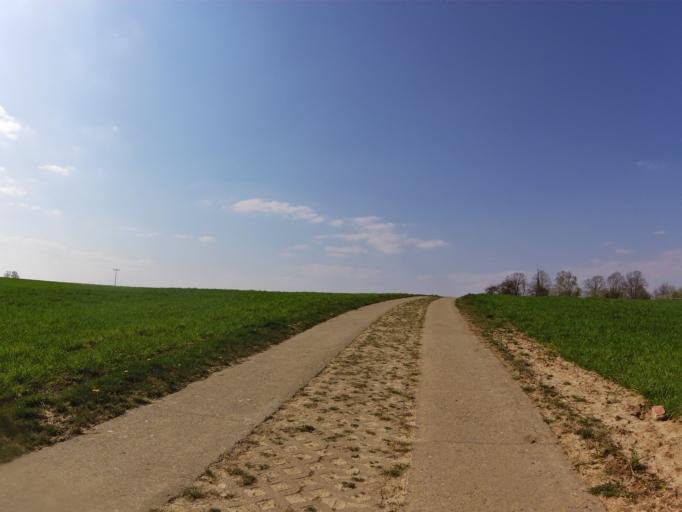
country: DE
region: Bavaria
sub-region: Regierungsbezirk Unterfranken
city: Prosselsheim
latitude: 49.8193
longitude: 10.1121
